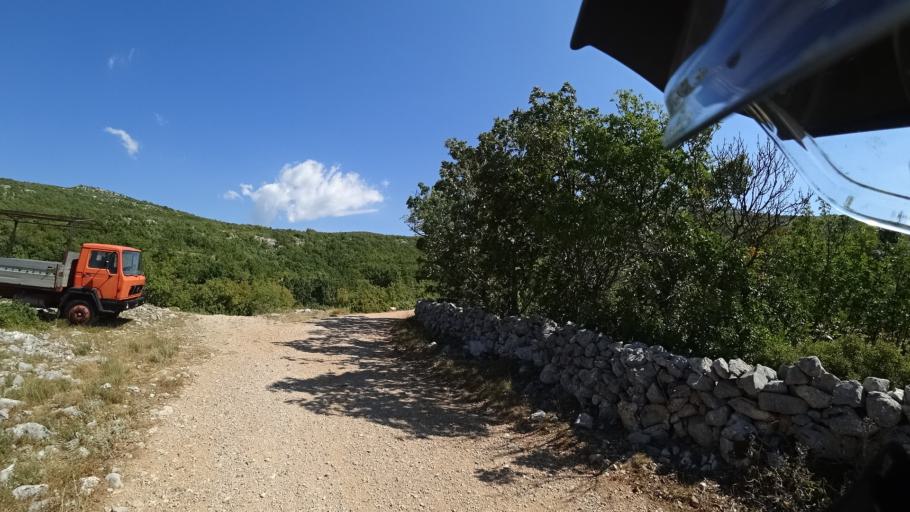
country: HR
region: Sibensko-Kniniska
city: Drnis
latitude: 43.8125
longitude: 16.3836
